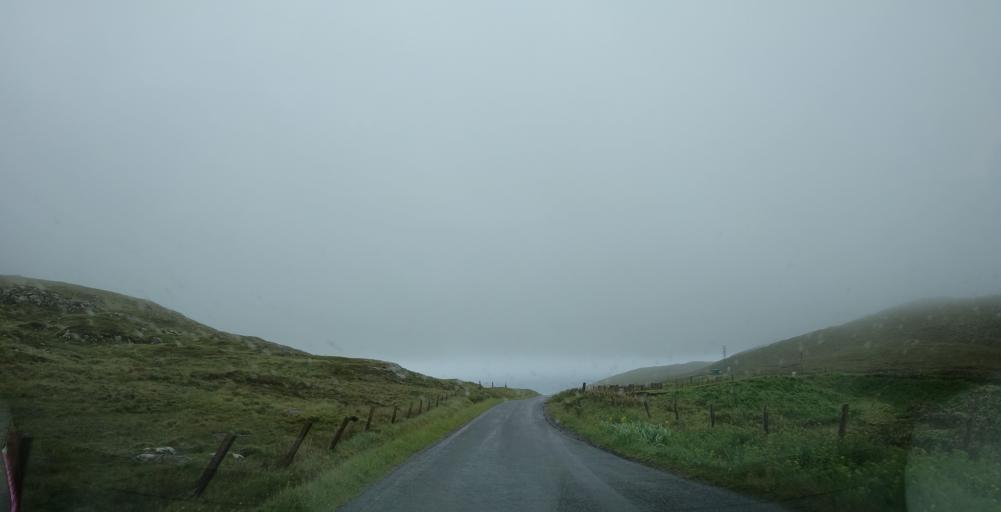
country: GB
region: Scotland
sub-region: Eilean Siar
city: Barra
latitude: 56.9601
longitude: -7.4641
